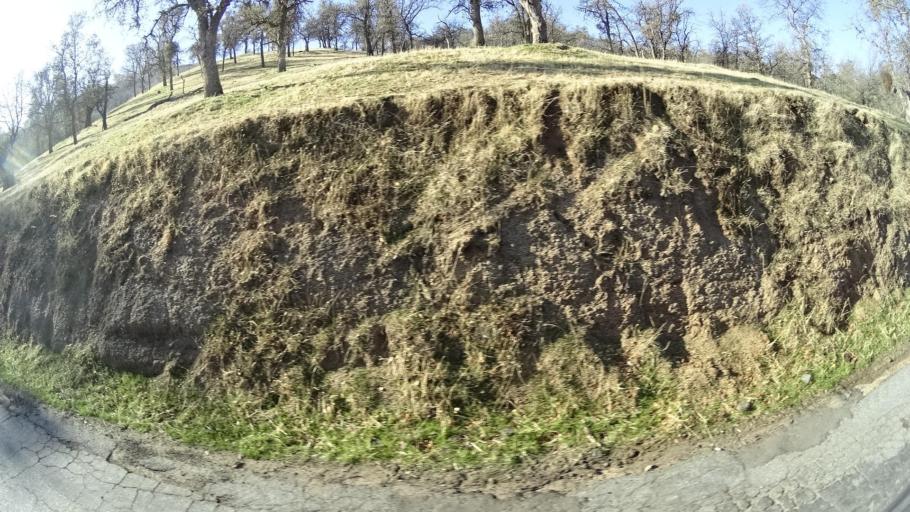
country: US
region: California
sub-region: Kern County
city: Alta Sierra
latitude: 35.7681
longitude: -118.8255
